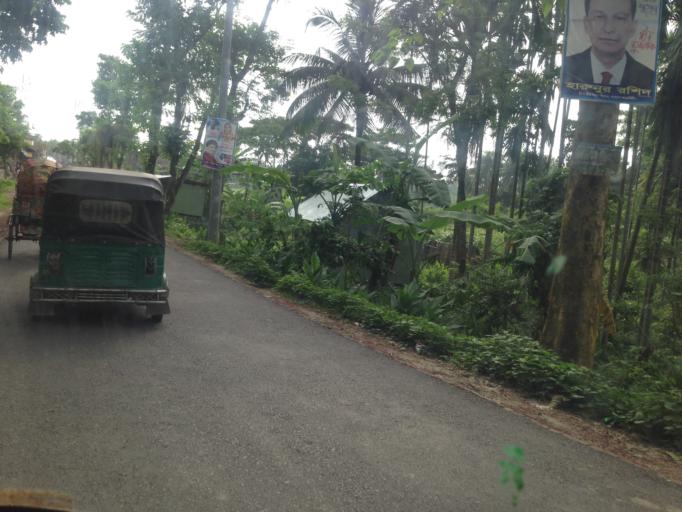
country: BD
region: Chittagong
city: Raipur
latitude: 23.0344
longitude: 90.7167
